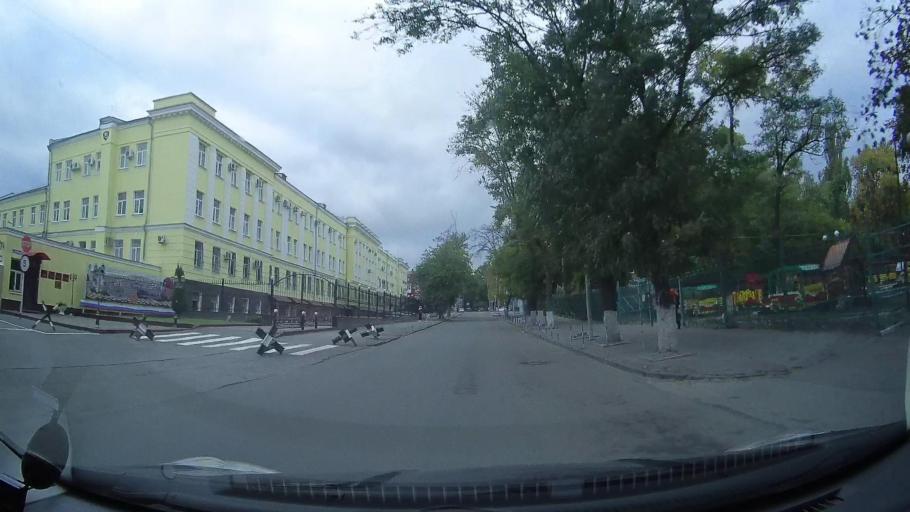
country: RU
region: Rostov
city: Rostov-na-Donu
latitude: 47.2354
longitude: 39.6950
